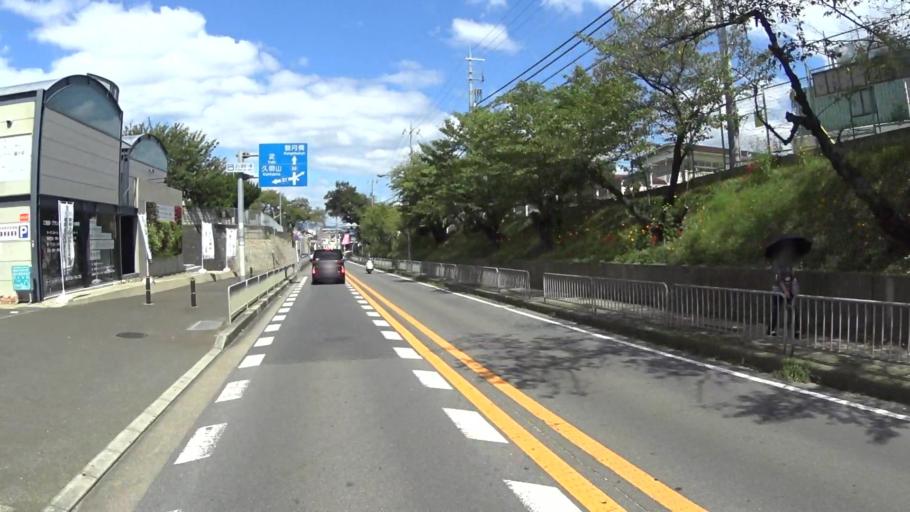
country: JP
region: Kyoto
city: Uji
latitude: 34.8879
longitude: 135.7820
